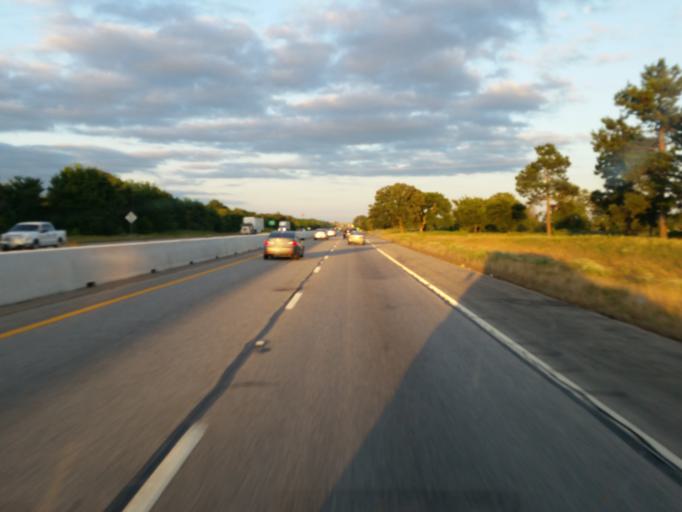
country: US
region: Texas
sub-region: Van Zandt County
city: Van
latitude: 32.5119
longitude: -95.6731
